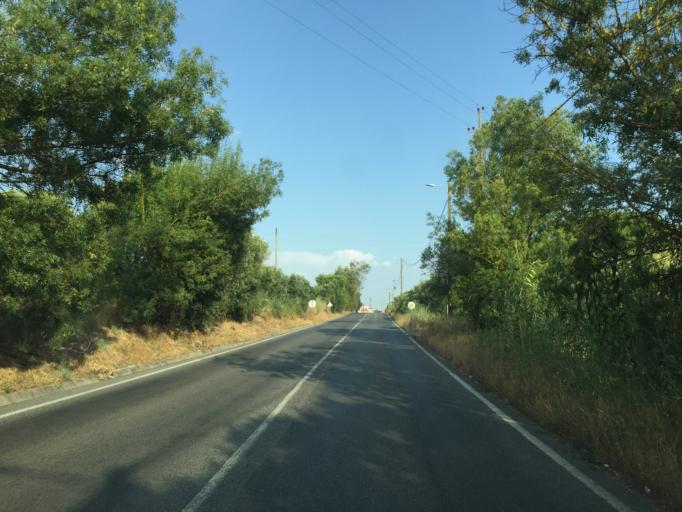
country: PT
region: Santarem
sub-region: Torres Novas
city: Torres Novas
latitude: 39.4799
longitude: -8.5725
